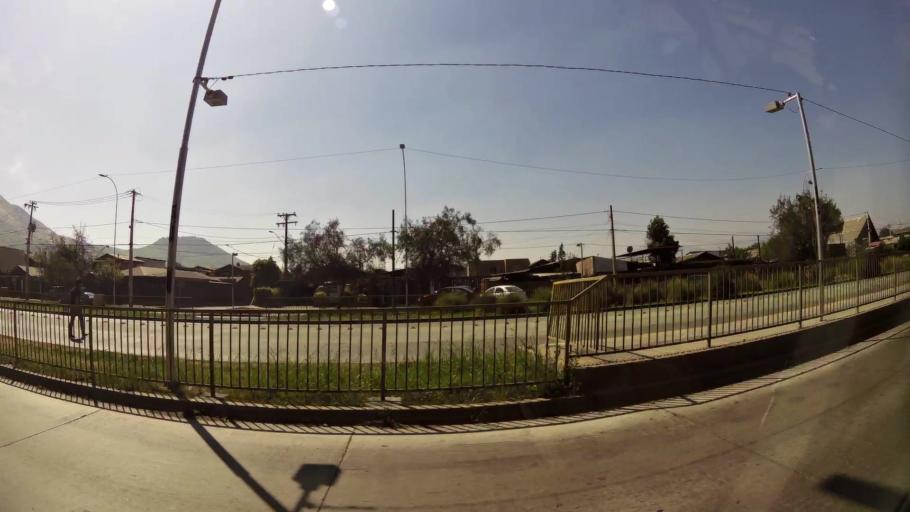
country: CL
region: Santiago Metropolitan
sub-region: Provincia de Santiago
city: Lo Prado
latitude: -33.4002
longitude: -70.6951
